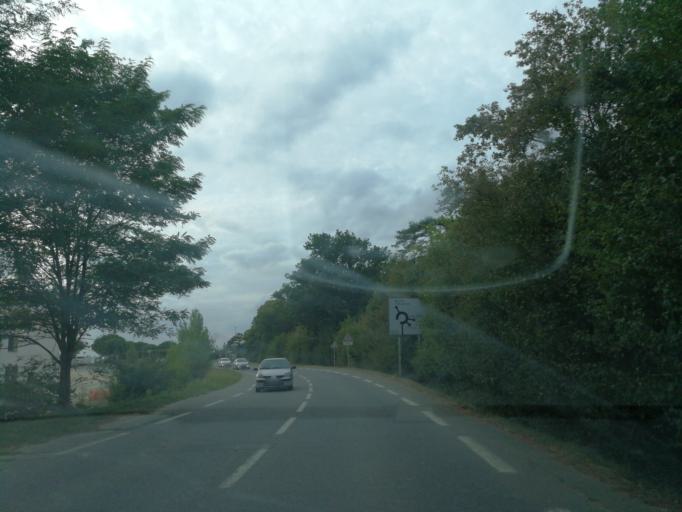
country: FR
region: Midi-Pyrenees
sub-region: Departement de la Haute-Garonne
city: Balma
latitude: 43.6117
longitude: 1.5286
